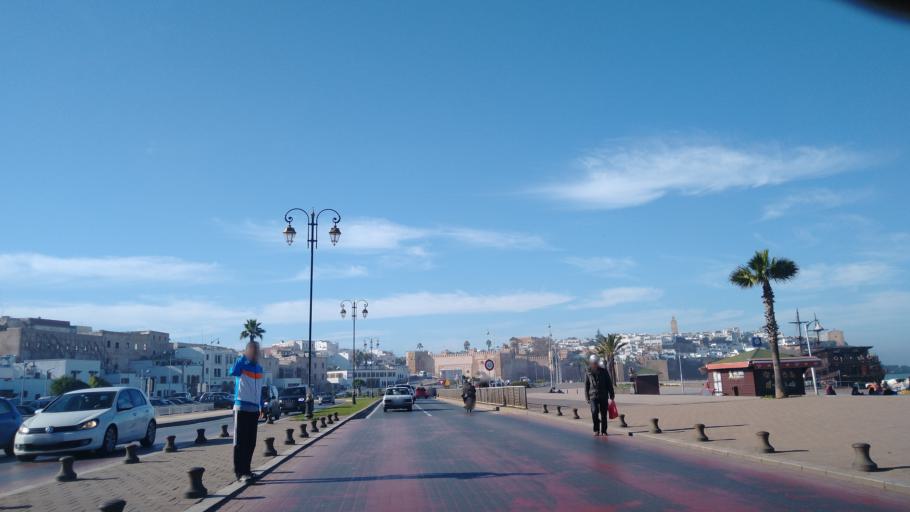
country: MA
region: Rabat-Sale-Zemmour-Zaer
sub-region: Rabat
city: Rabat
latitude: 34.0278
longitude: -6.8315
